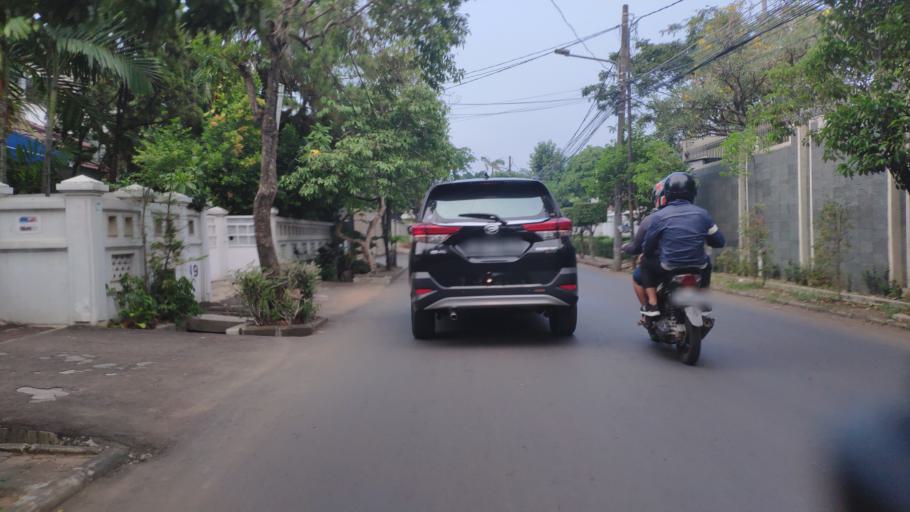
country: ID
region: West Java
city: Pamulang
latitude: -6.3003
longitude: 106.7985
